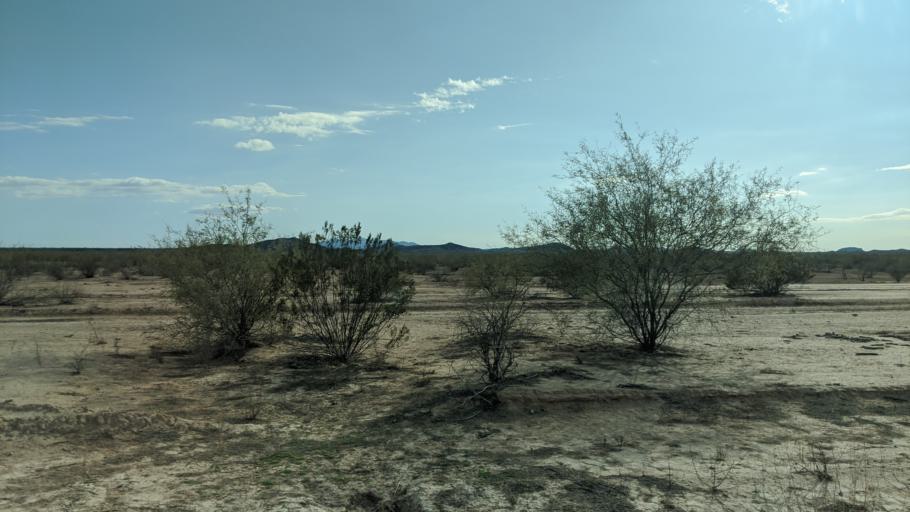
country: MX
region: Sonora
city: Sonoyta
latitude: 32.0940
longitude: -113.4432
